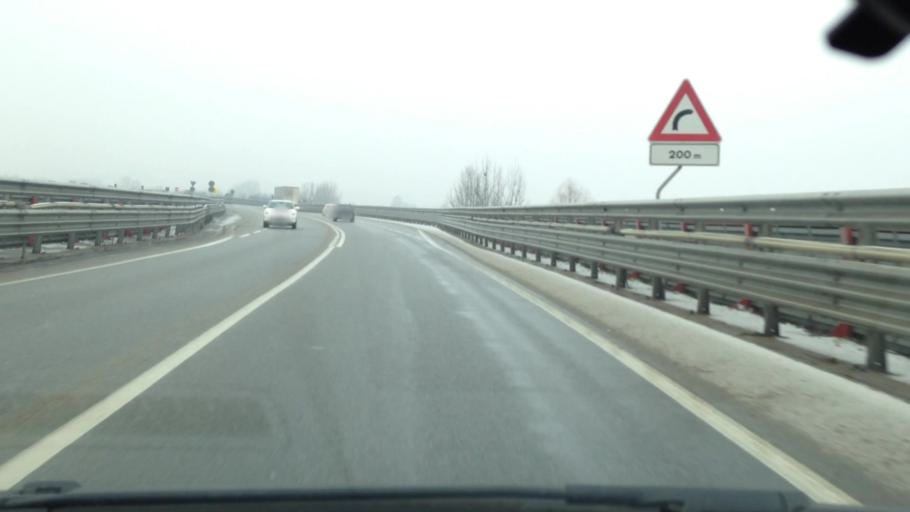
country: IT
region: Piedmont
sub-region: Provincia di Asti
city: Isola d'Asti
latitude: 44.8428
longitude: 8.1920
